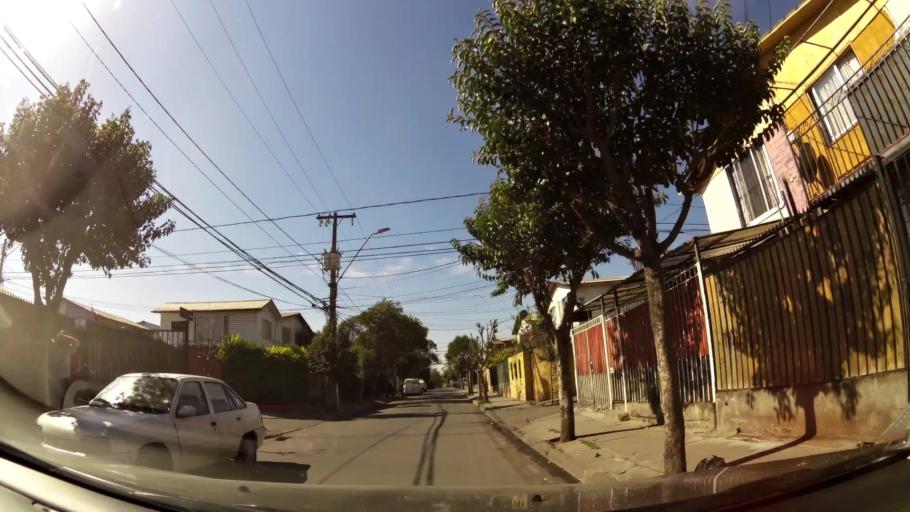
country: CL
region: Santiago Metropolitan
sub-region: Provincia de Maipo
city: San Bernardo
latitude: -33.6141
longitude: -70.7050
